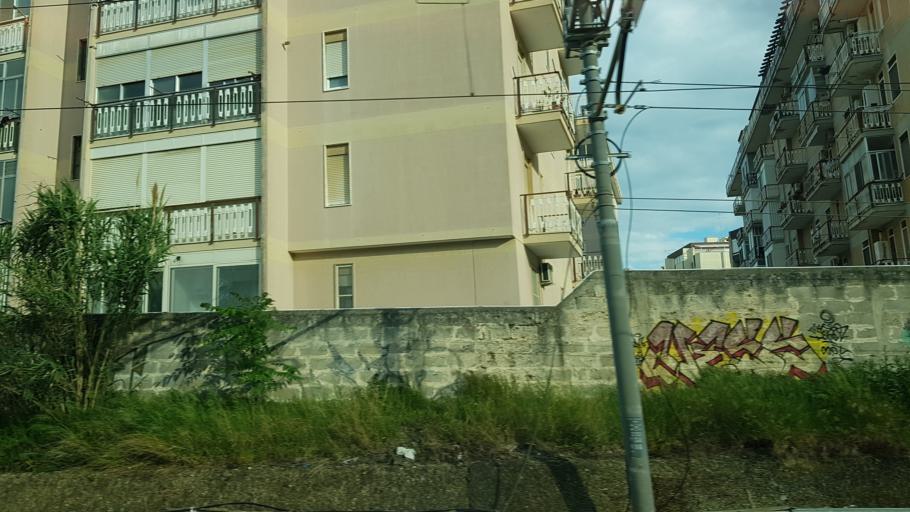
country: IT
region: Apulia
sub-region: Provincia di Brindisi
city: Brindisi
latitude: 40.6365
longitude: 17.9292
